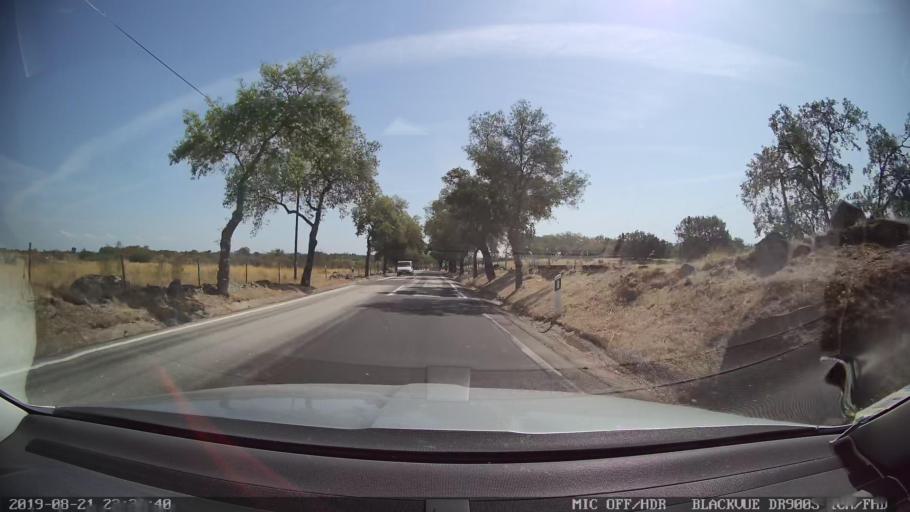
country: PT
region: Guarda
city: Alcains
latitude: 39.8749
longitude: -7.4260
